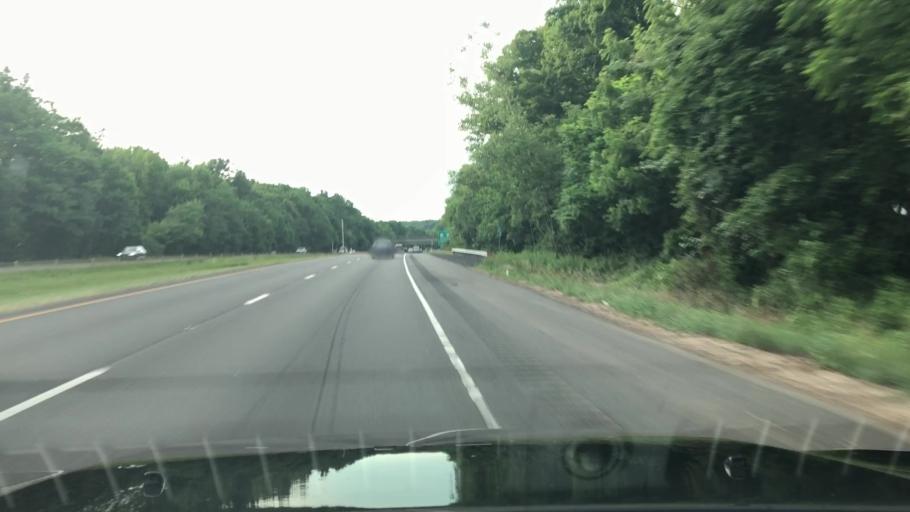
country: US
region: Pennsylvania
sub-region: Bucks County
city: Hulmeville
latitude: 40.1529
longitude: -74.8990
